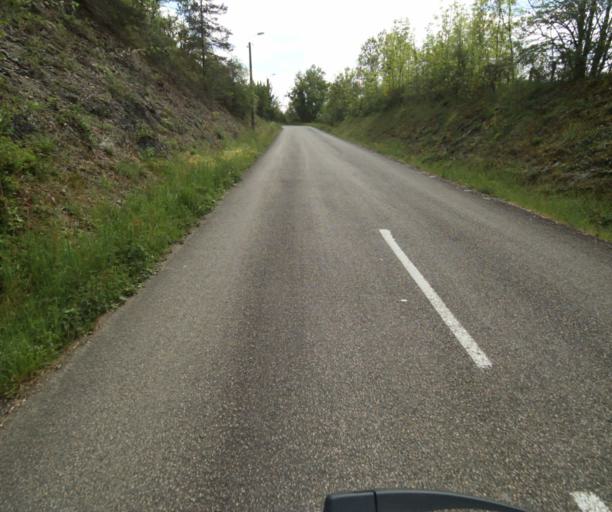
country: FR
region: Limousin
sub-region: Departement de la Correze
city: Tulle
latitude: 45.2682
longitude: 1.7631
